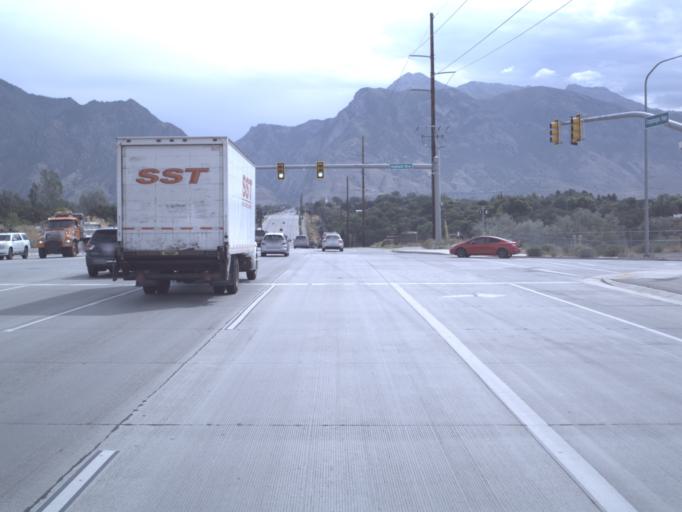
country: US
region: Utah
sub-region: Utah County
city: Lehi
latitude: 40.4316
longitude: -111.8223
